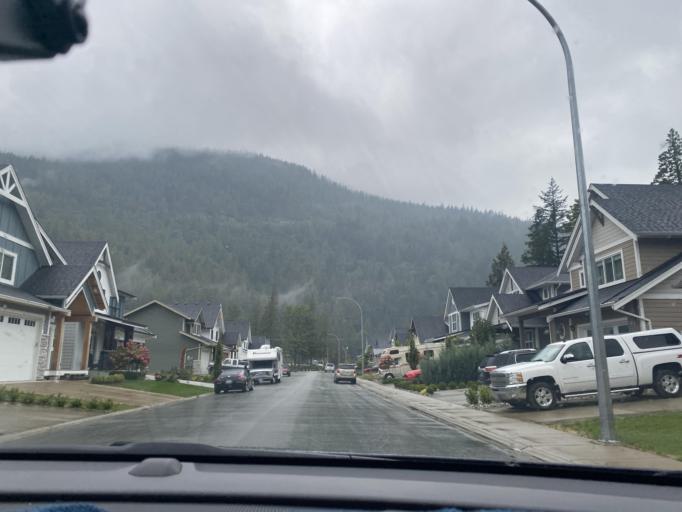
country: CA
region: British Columbia
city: Agassiz
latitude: 49.2929
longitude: -121.7783
